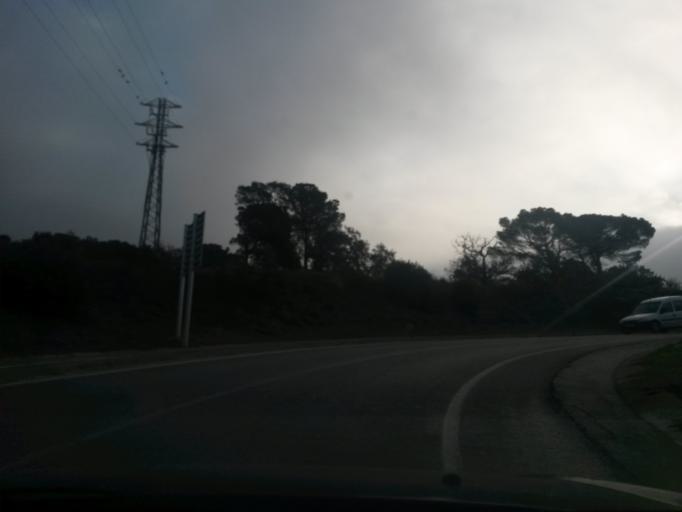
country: ES
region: Catalonia
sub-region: Provincia de Girona
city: Llagostera
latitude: 41.8308
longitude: 2.9088
